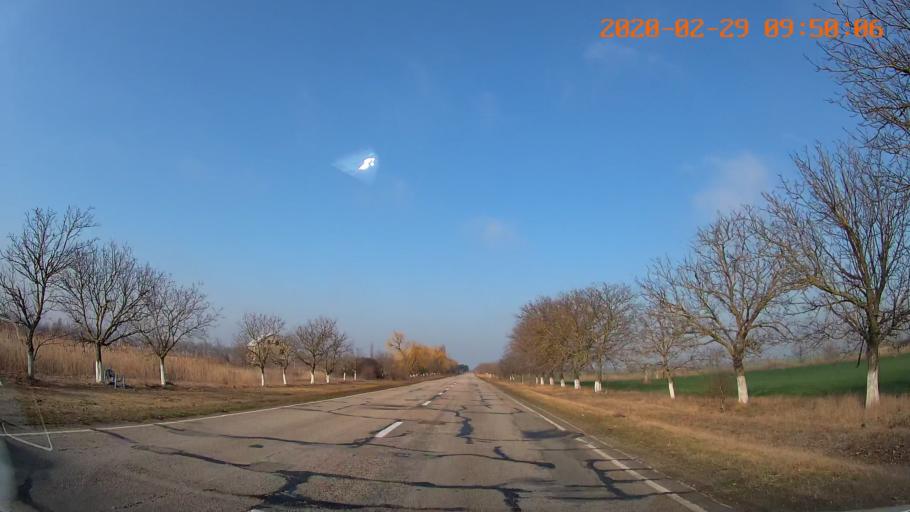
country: MD
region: Telenesti
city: Slobozia
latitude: 46.7011
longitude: 29.7617
